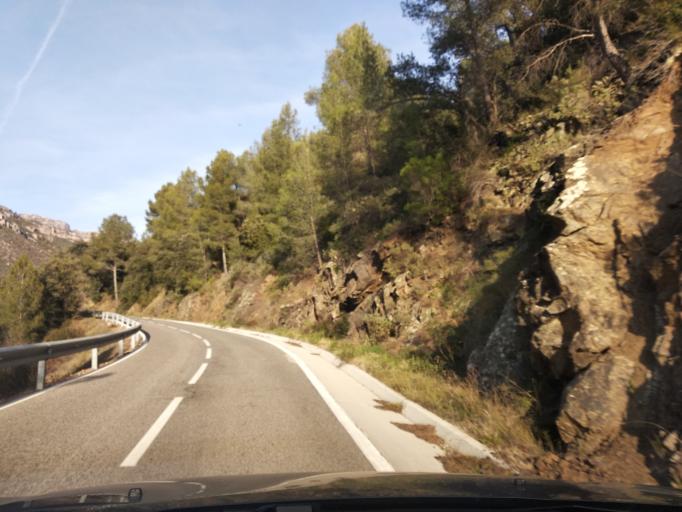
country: ES
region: Catalonia
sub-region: Provincia de Tarragona
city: Margalef
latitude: 41.2388
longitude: 0.7869
